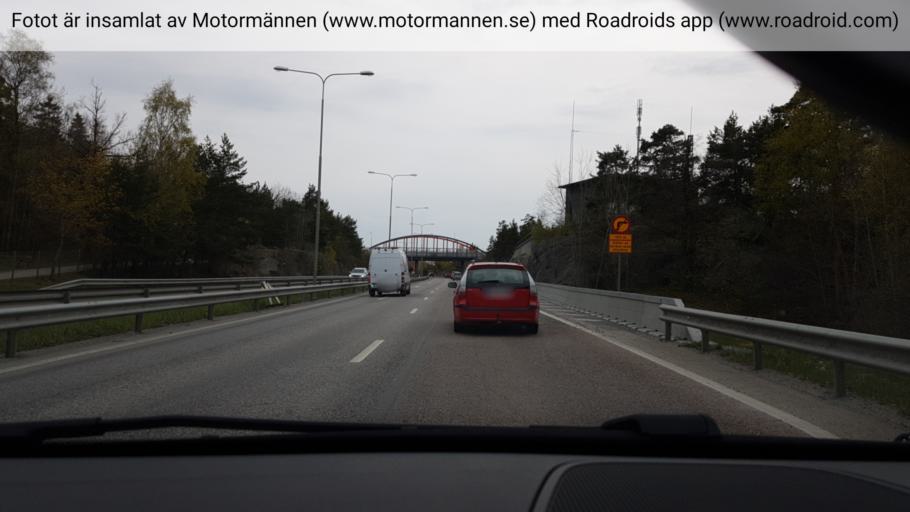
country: SE
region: Stockholm
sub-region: Stockholms Kommun
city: Arsta
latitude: 59.2894
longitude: 18.0225
